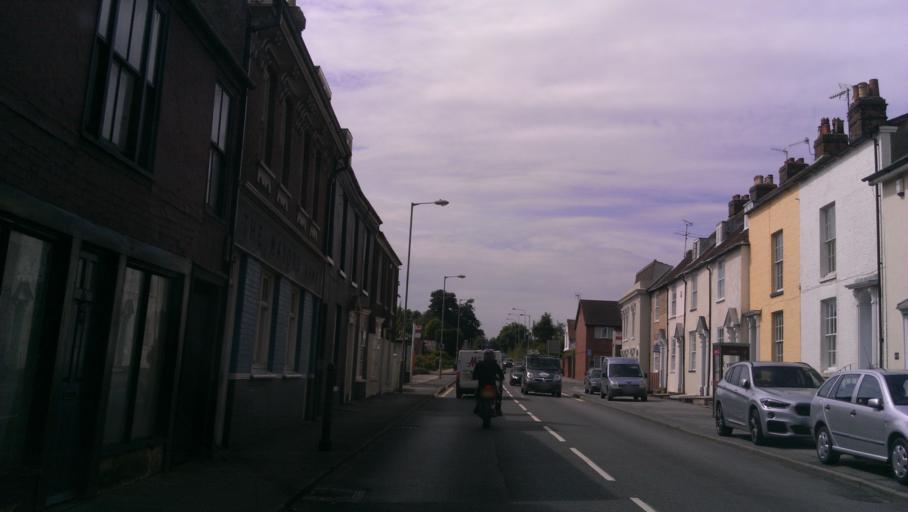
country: GB
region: England
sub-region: Kent
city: Faversham
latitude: 51.3118
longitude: 0.8720
